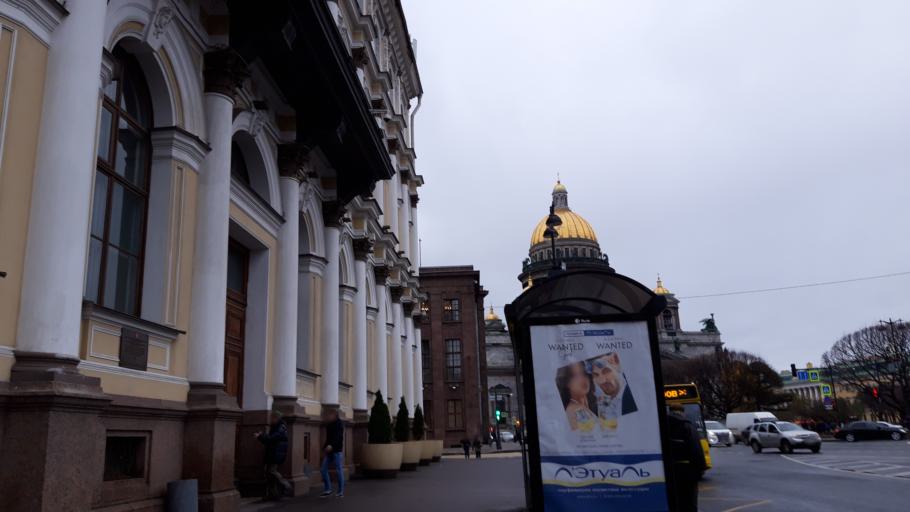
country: RU
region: St.-Petersburg
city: Saint Petersburg
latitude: 59.9317
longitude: 30.3075
